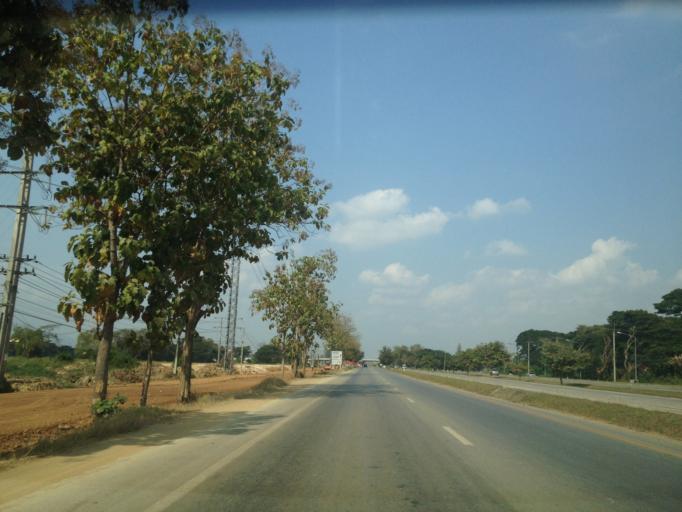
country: TH
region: Chiang Mai
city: Saraphi
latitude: 18.7296
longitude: 99.0392
